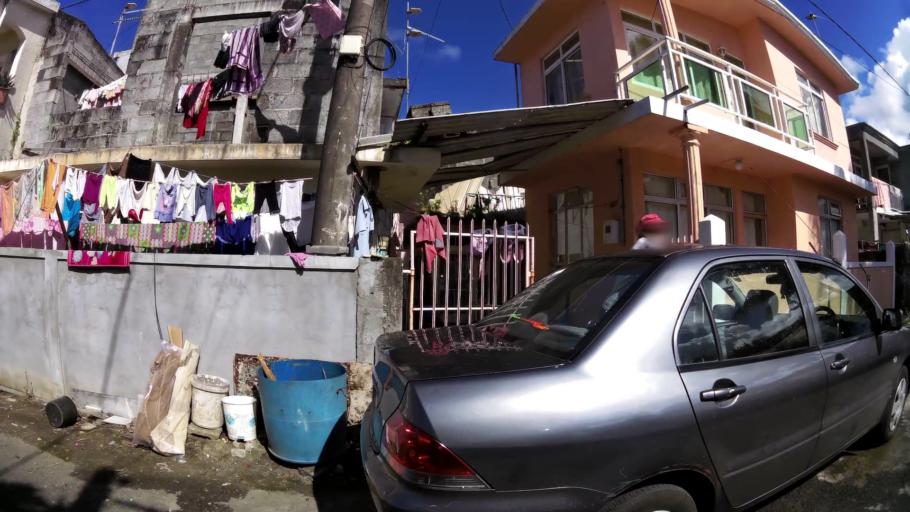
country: MU
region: Grand Port
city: Plaine Magnien
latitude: -20.4348
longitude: 57.6601
